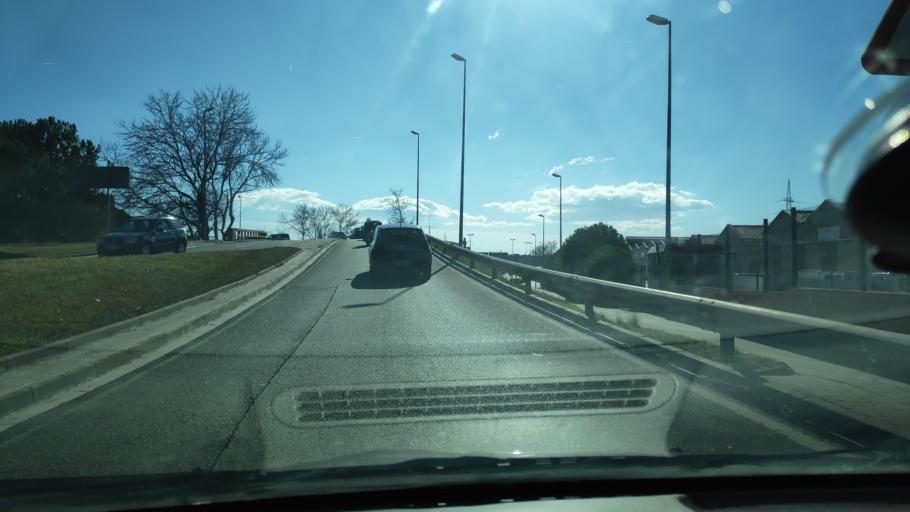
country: ES
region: Catalonia
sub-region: Provincia de Barcelona
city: Terrassa
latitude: 41.5570
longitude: 2.0389
